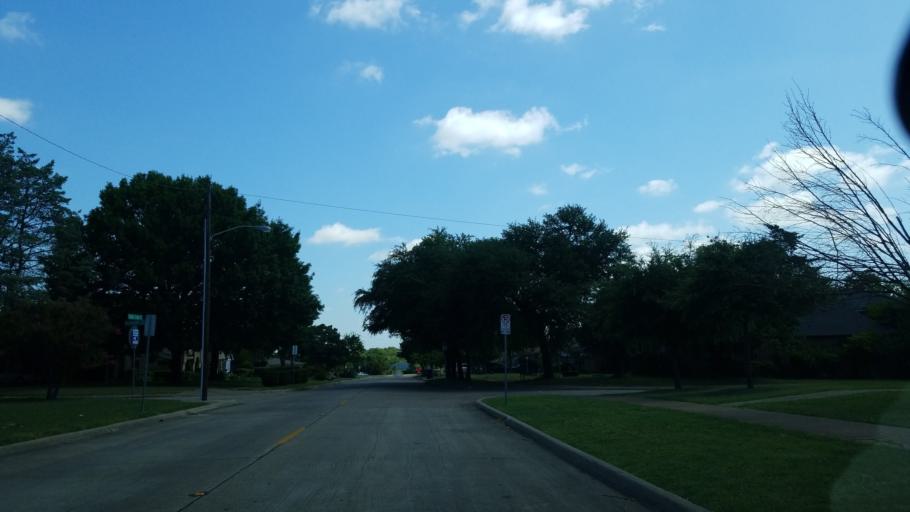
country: US
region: Texas
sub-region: Dallas County
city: Dallas
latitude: 32.7289
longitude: -96.7956
